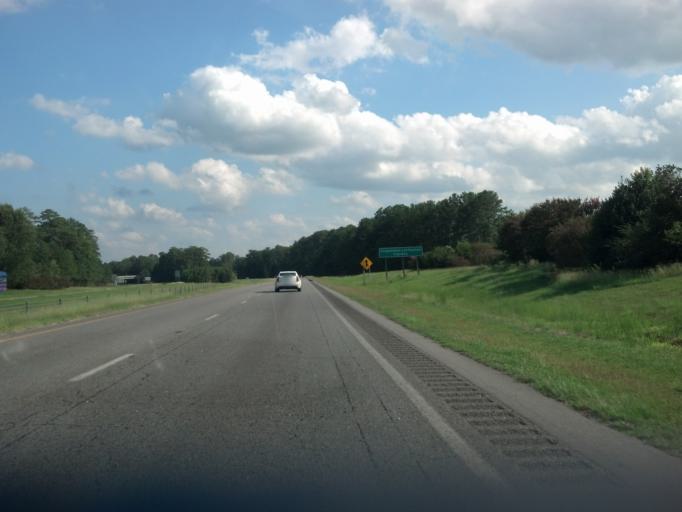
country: US
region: North Carolina
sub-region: Nash County
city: Rocky Mount
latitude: 35.9455
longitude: -77.7596
